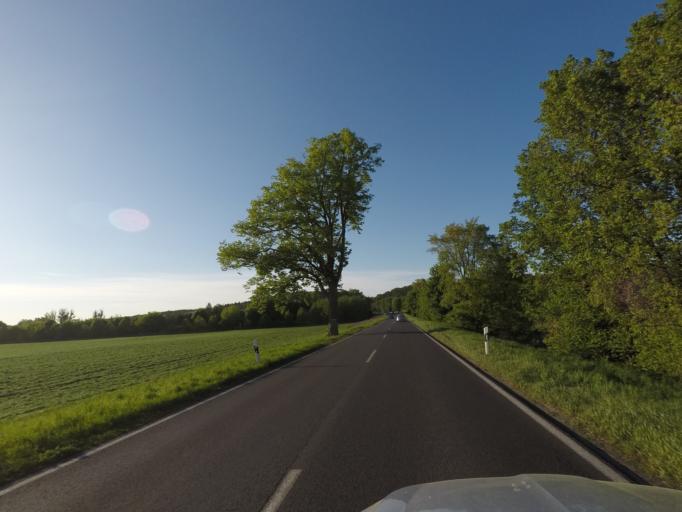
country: DE
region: Brandenburg
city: Bad Freienwalde
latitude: 52.8021
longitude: 14.0459
